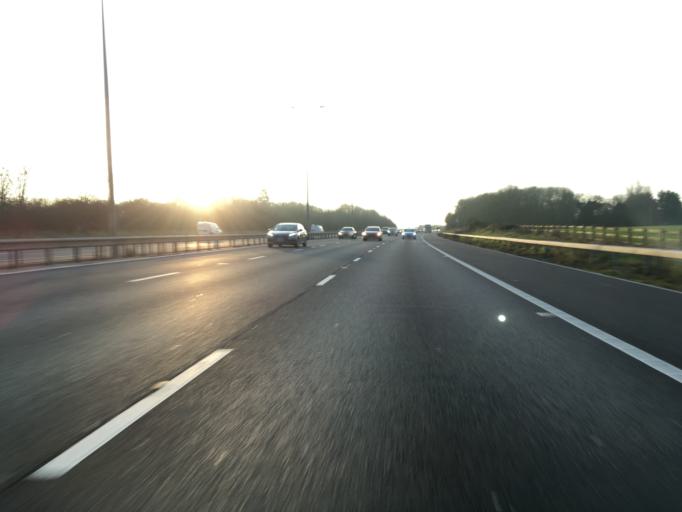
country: GB
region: England
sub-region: Worcestershire
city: Upton upon Severn
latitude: 52.1001
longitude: -2.1874
